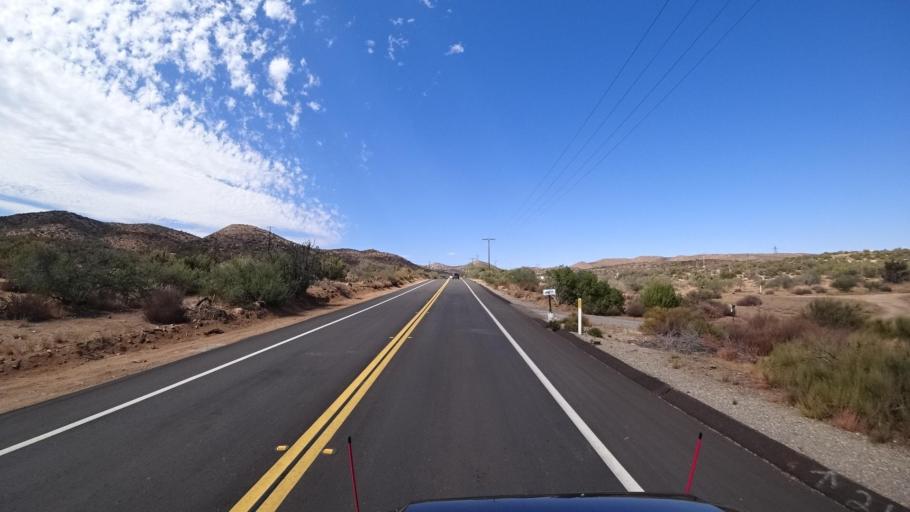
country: MX
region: Baja California
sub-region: Tecate
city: Cereso del Hongo
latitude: 32.6284
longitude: -116.2231
